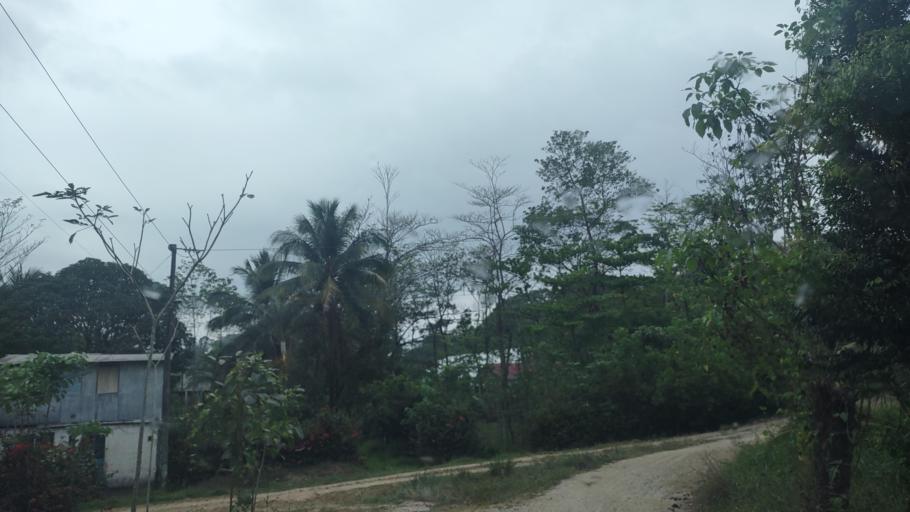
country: MX
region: Veracruz
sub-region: Uxpanapa
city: Poblado 10
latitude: 17.4504
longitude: -94.0970
